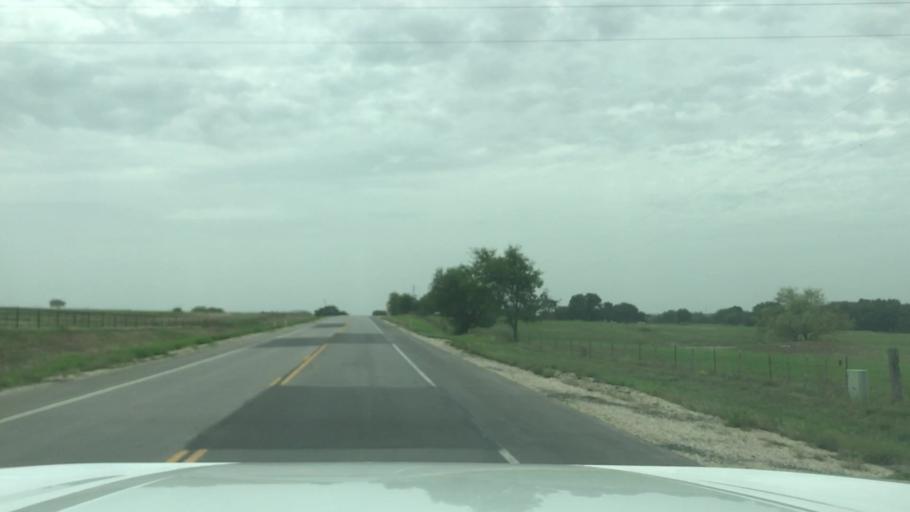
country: US
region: Texas
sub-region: Erath County
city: Dublin
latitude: 32.0663
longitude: -98.2170
